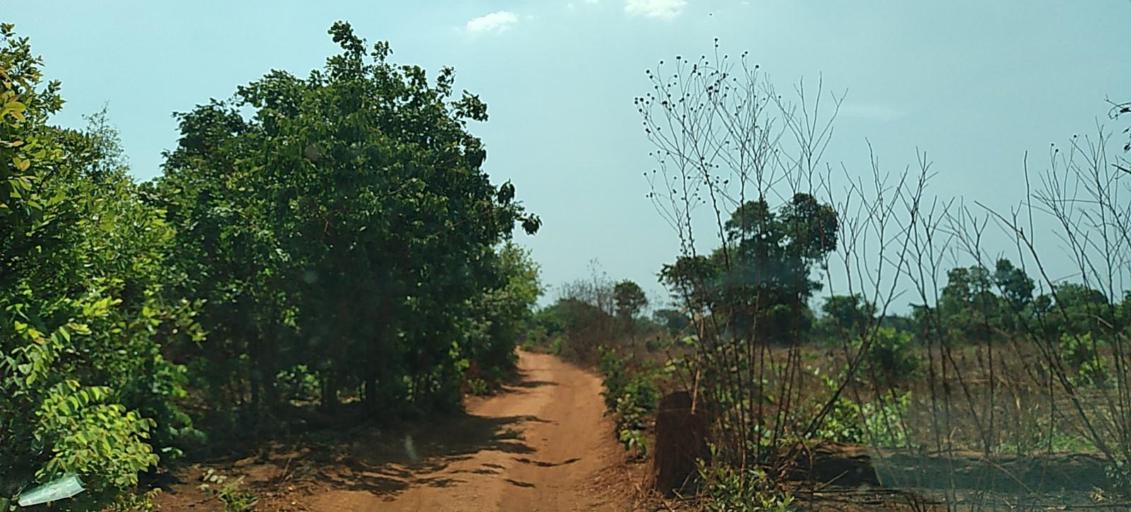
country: ZM
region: North-Western
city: Solwezi
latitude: -12.1263
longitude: 26.3074
